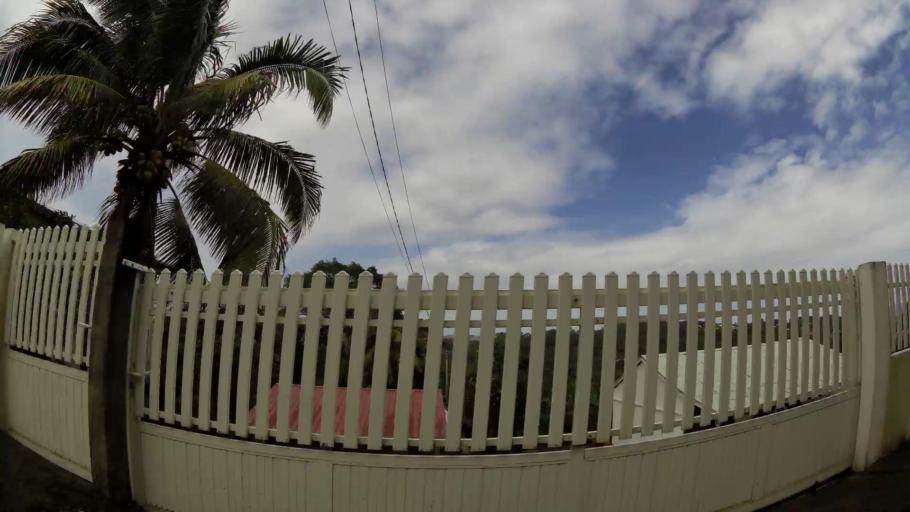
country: MQ
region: Martinique
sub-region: Martinique
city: Saint-Joseph
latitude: 14.6535
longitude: -61.0358
